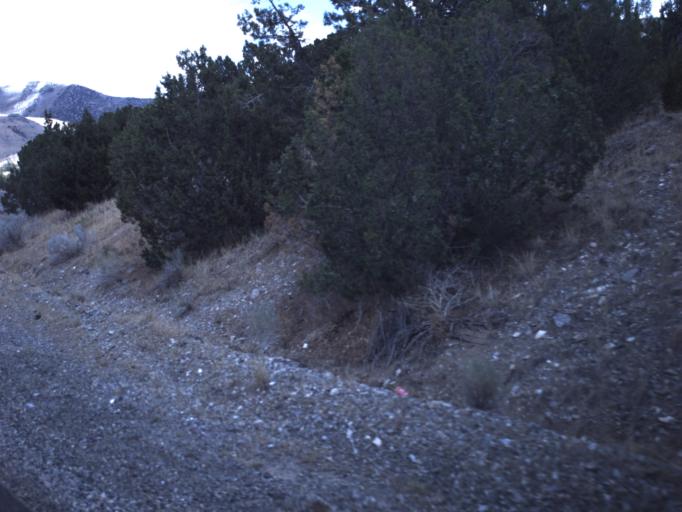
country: US
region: Utah
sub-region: Tooele County
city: Grantsville
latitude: 40.3260
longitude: -112.6238
